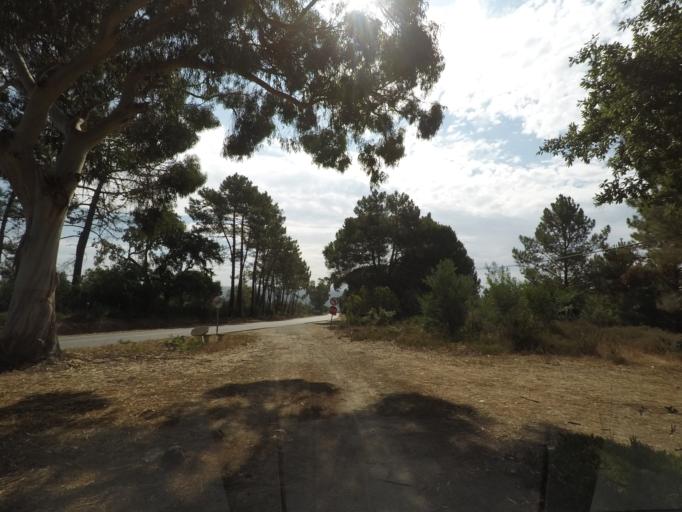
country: PT
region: Beja
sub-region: Odemira
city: Sao Teotonio
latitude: 37.4463
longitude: -8.7615
